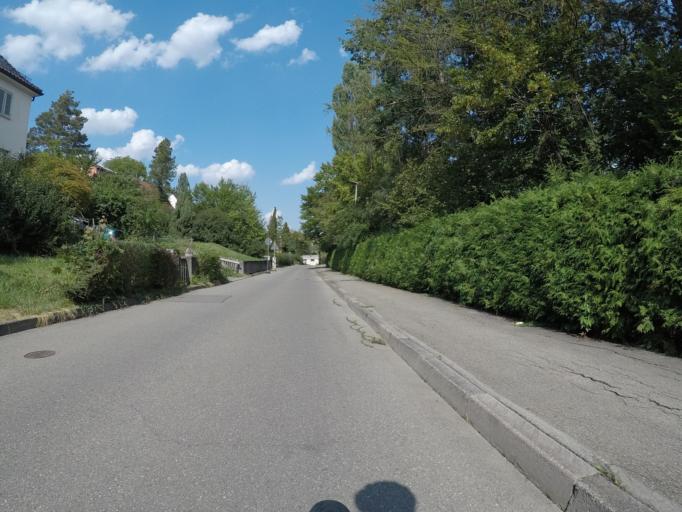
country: DE
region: Baden-Wuerttemberg
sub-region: Tuebingen Region
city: Eningen unter Achalm
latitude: 48.4866
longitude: 9.2533
